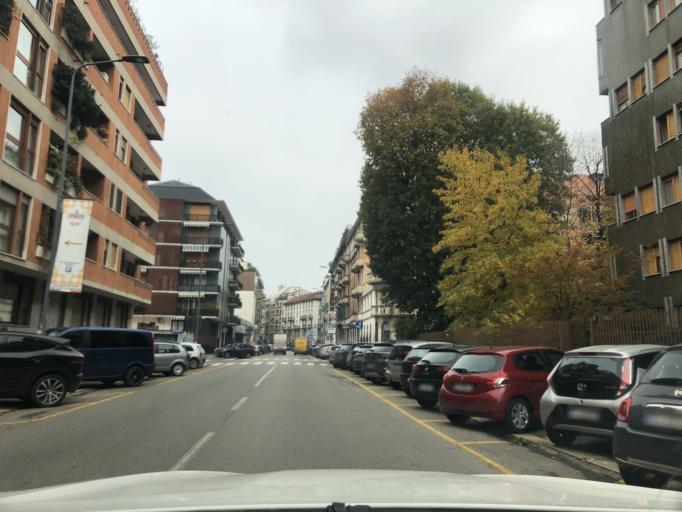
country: IT
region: Lombardy
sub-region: Citta metropolitana di Milano
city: Milano
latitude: 45.4568
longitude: 9.2094
